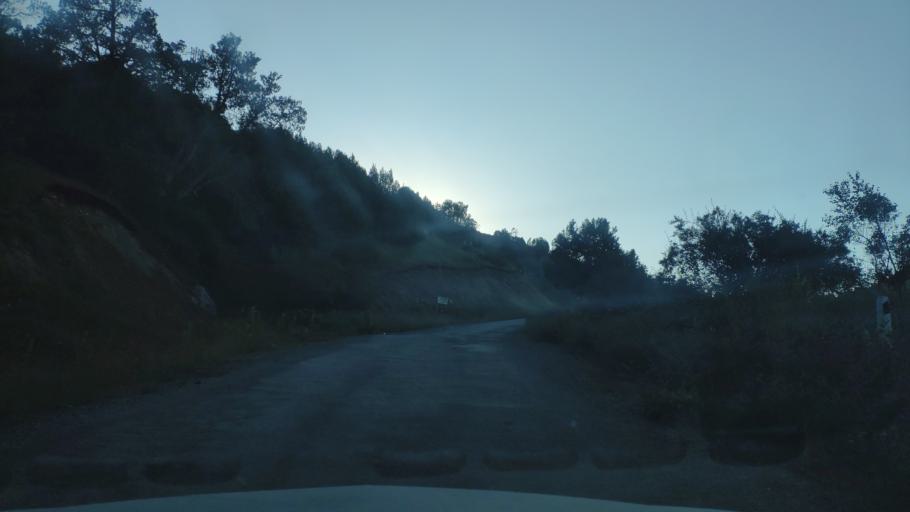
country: TJ
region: Viloyati Sughd
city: Ayni
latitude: 39.6394
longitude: 68.4742
